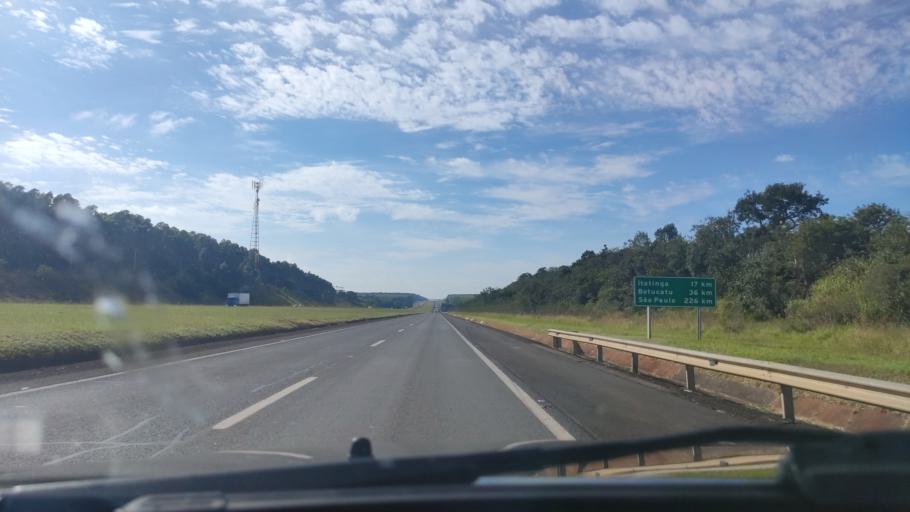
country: BR
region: Sao Paulo
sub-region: Itatinga
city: Itatinga
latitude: -23.0197
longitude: -48.6774
